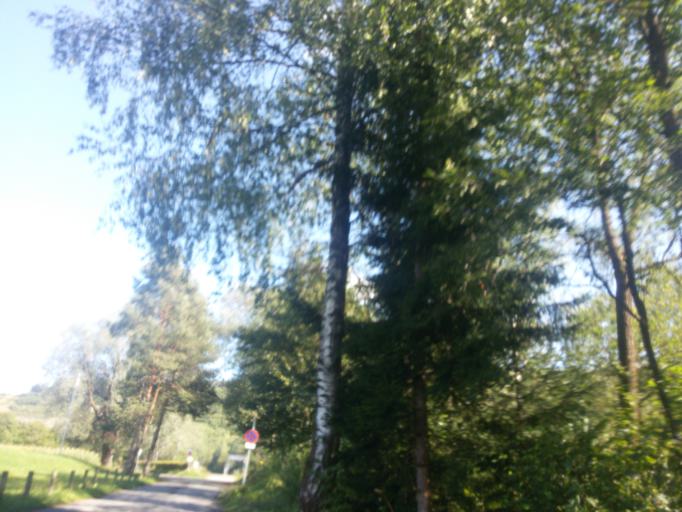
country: AT
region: Carinthia
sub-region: Politischer Bezirk Villach Land
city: Wernberg
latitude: 46.6069
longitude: 13.9058
